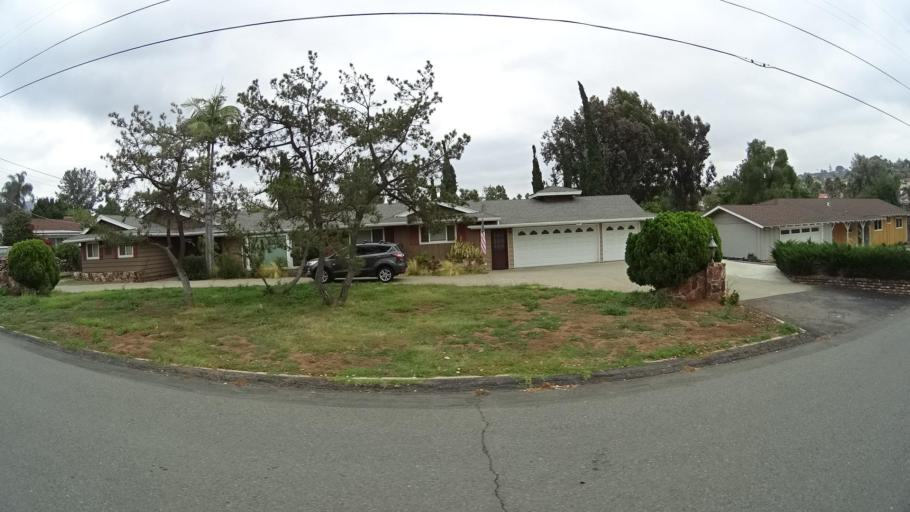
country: US
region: California
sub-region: San Diego County
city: Spring Valley
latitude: 32.7457
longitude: -116.9952
